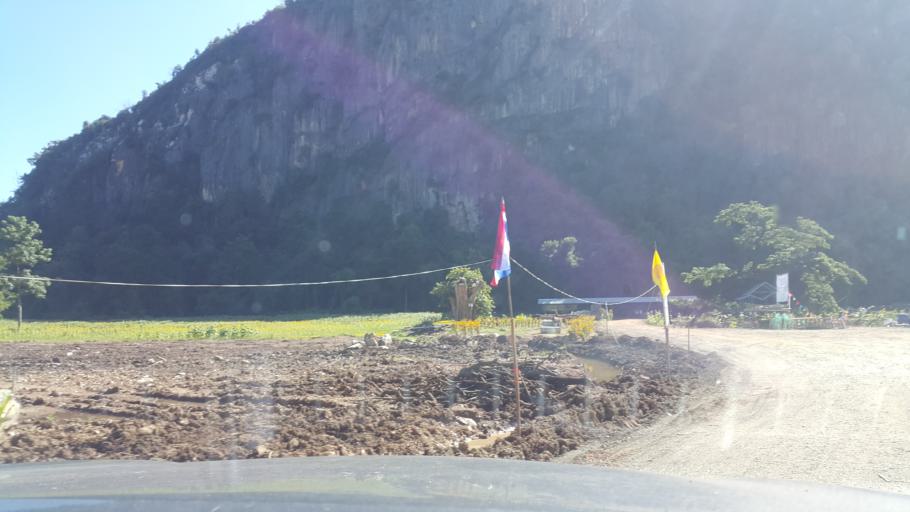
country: TH
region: Sukhothai
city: Thung Saliam
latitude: 17.3335
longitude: 99.5071
